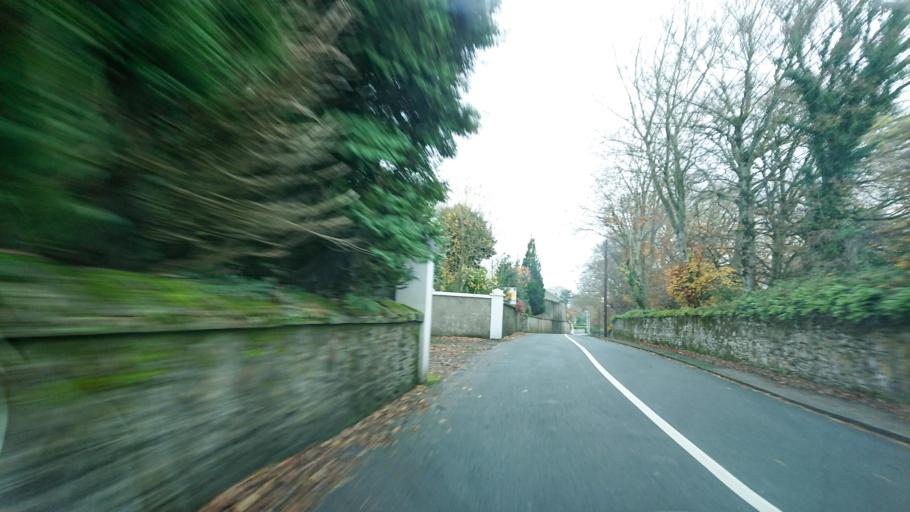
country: IE
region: Munster
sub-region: South Tipperary
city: Cluain Meala
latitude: 52.3521
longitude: -7.6828
